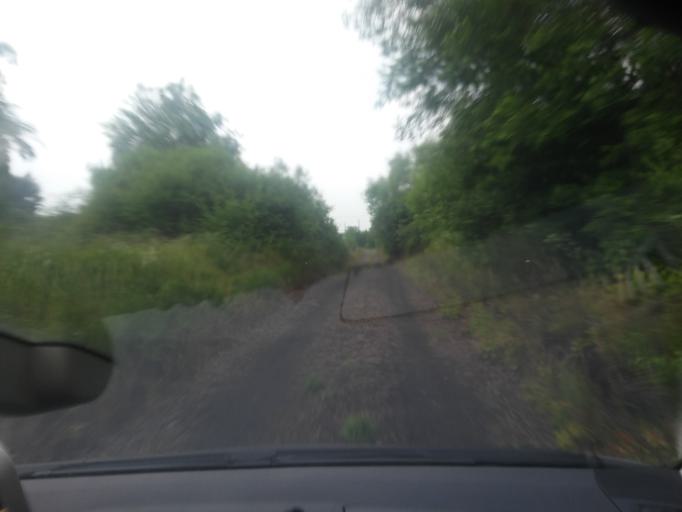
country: BE
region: Wallonia
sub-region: Province du Luxembourg
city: Arlon
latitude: 49.6907
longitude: 5.7562
